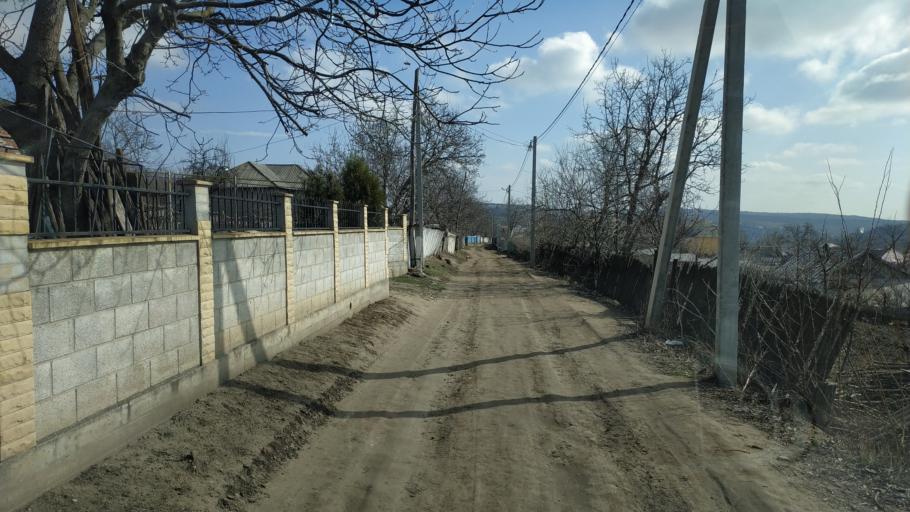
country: MD
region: Hincesti
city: Hincesti
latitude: 46.8298
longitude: 28.6671
